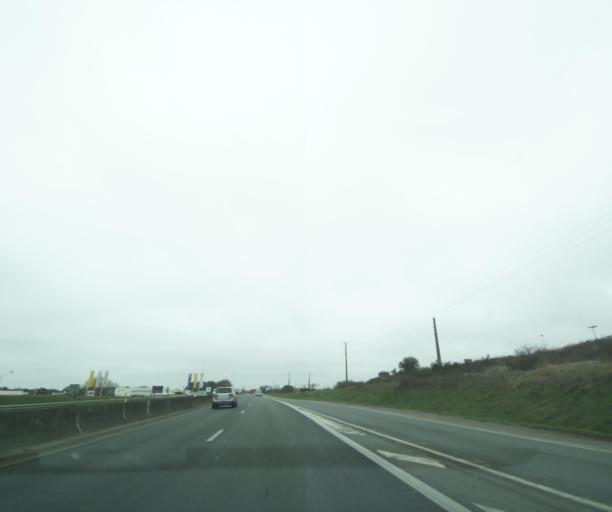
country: FR
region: Poitou-Charentes
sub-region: Departement de la Charente-Maritime
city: Perigny
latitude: 46.1558
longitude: -1.1159
